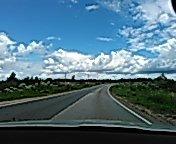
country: RU
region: Moskovskaya
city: Shevlyakovo
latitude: 56.5189
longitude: 36.7408
